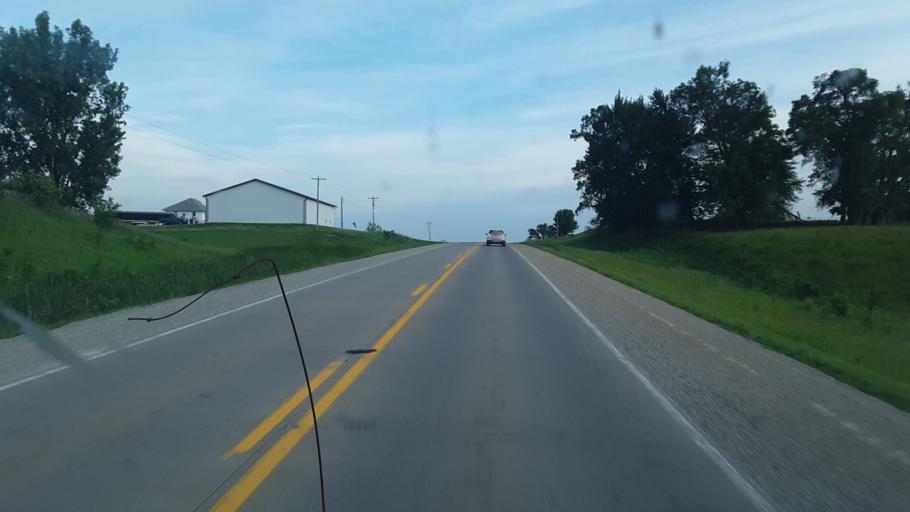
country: US
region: Iowa
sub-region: Benton County
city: Belle Plaine
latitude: 41.8290
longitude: -92.2786
